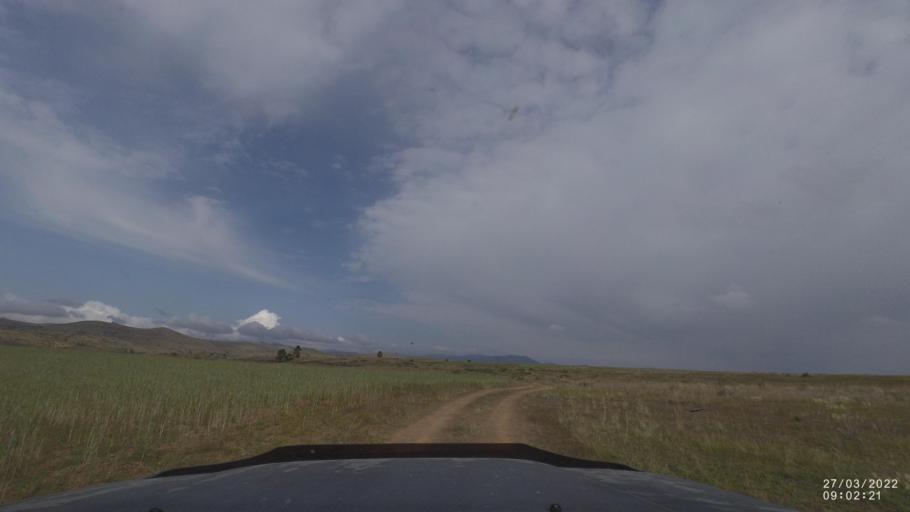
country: BO
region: Cochabamba
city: Cliza
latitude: -17.7371
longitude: -65.8574
